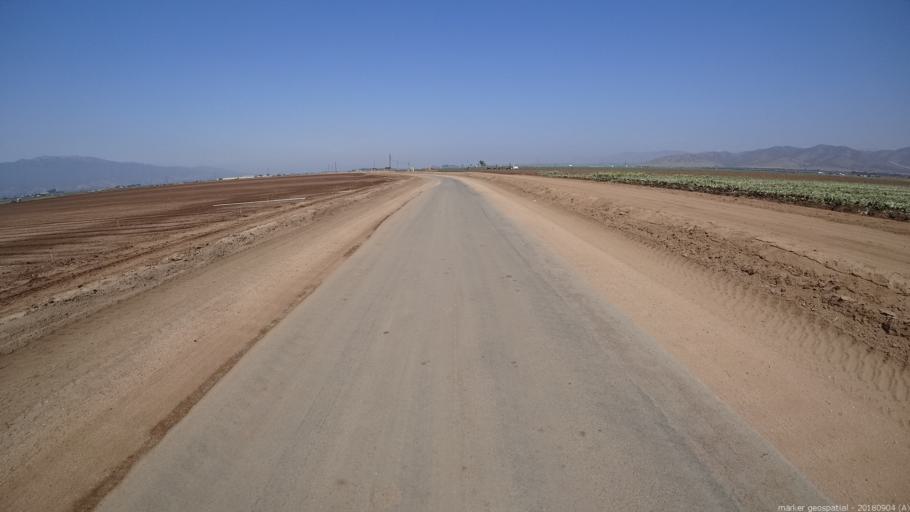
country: US
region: California
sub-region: Monterey County
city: Gonzales
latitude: 36.5295
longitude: -121.4443
